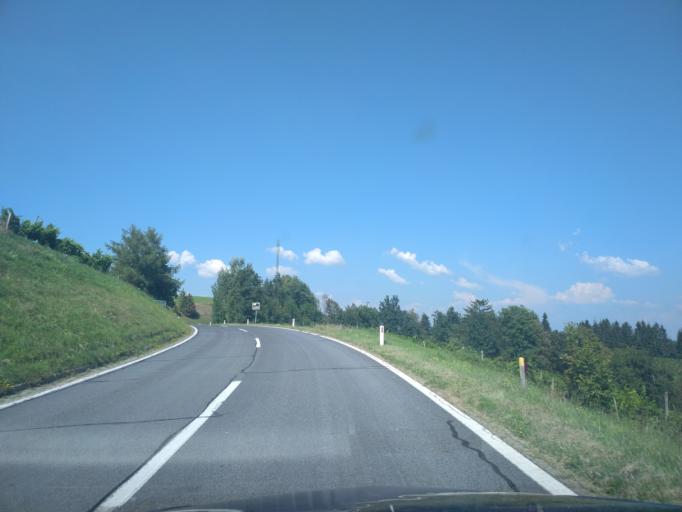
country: AT
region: Styria
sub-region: Politischer Bezirk Leibnitz
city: Leutschach
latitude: 46.6794
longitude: 15.4792
